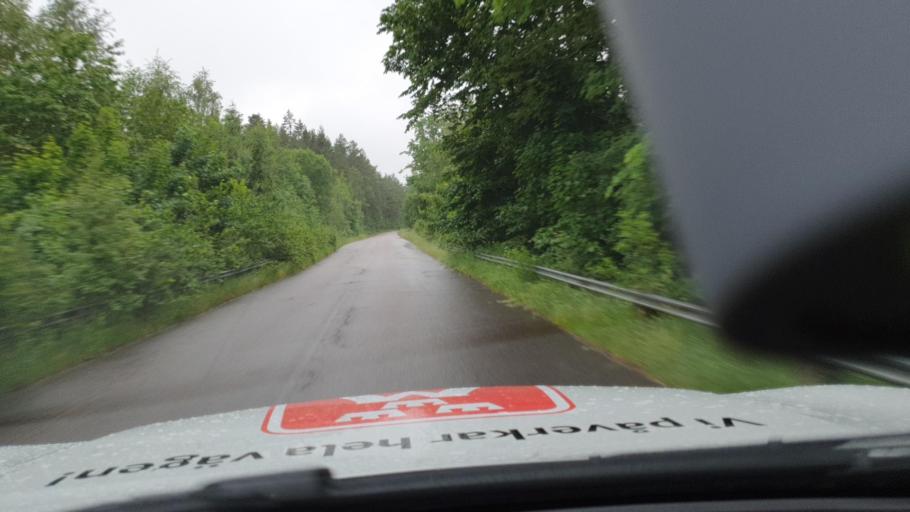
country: SE
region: Vaestra Goetaland
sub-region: Skovde Kommun
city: Stopen
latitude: 58.4310
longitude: 13.9222
